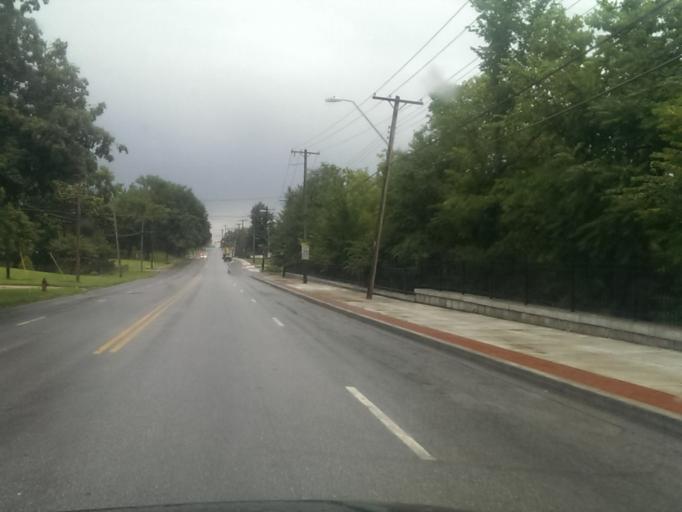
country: US
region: Kansas
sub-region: Johnson County
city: Leawood
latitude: 38.9636
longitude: -94.5816
